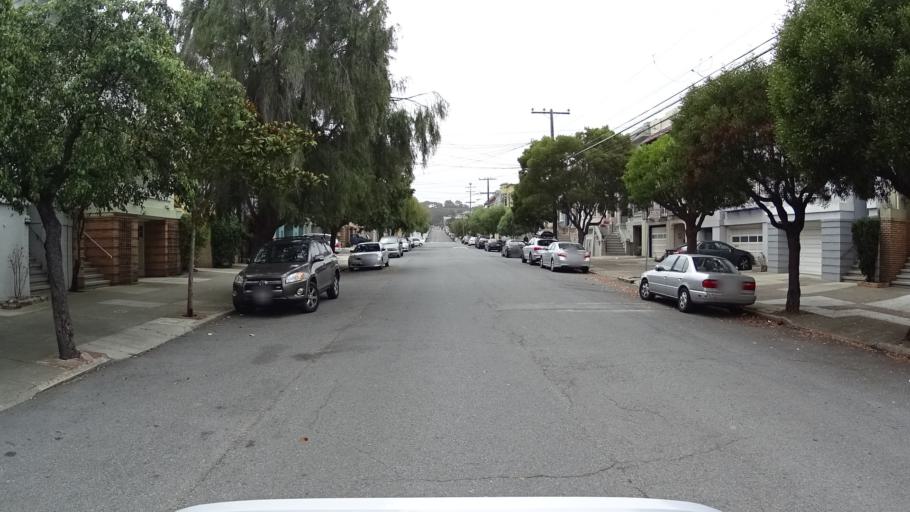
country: US
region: California
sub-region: San Francisco County
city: San Francisco
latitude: 37.7798
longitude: -122.4761
